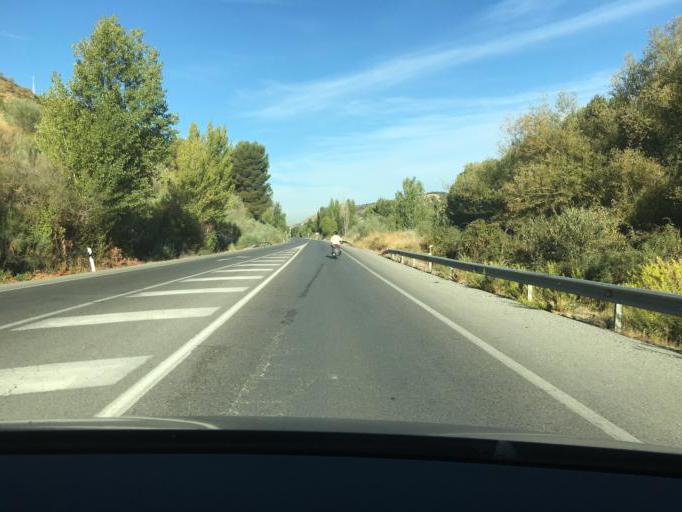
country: ES
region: Andalusia
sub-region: Provincia de Granada
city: Cenes de la Vega
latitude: 37.1571
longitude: -3.5484
